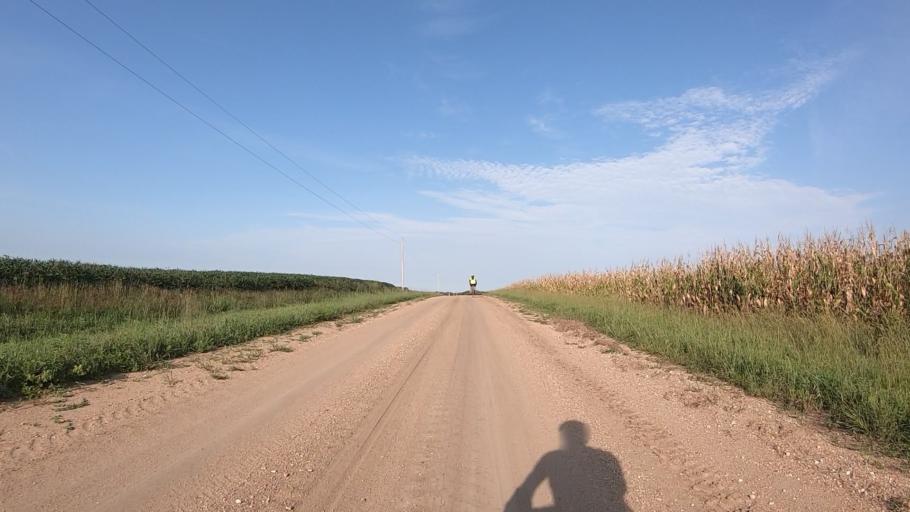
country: US
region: Kansas
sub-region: Marshall County
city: Blue Rapids
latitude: 39.6533
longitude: -96.8565
